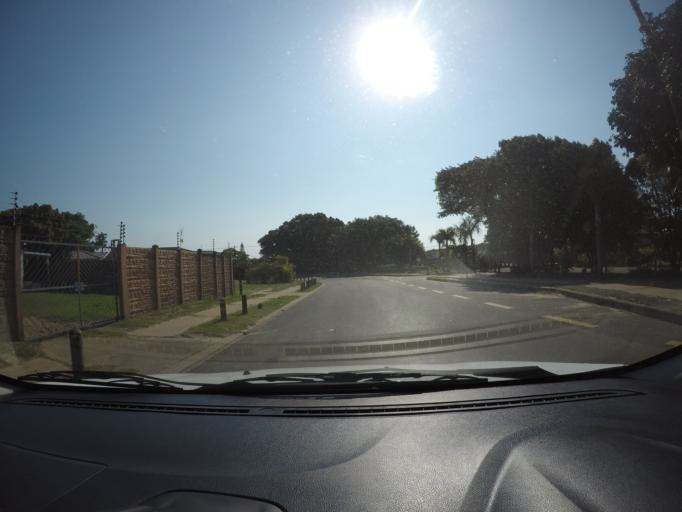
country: ZA
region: KwaZulu-Natal
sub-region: uThungulu District Municipality
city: Richards Bay
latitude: -28.7200
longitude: 32.0392
